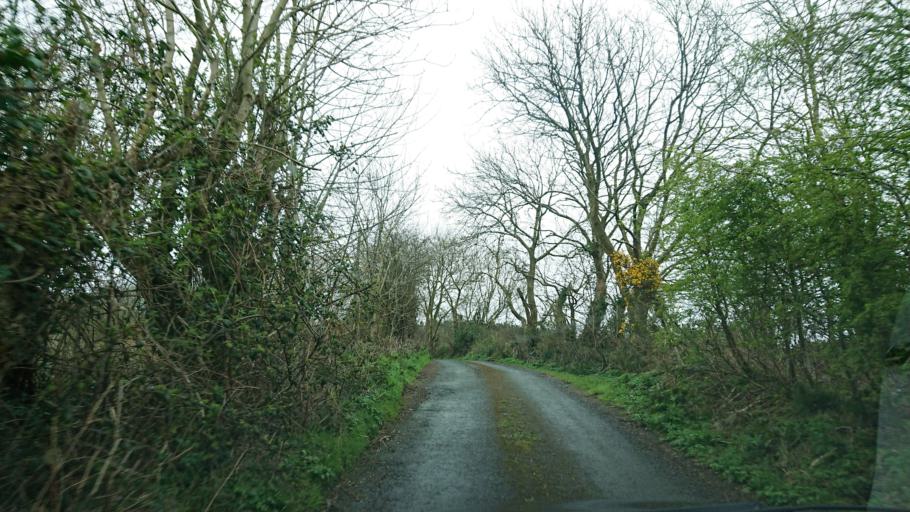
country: IE
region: Munster
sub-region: Waterford
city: Waterford
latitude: 52.2629
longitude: -7.0108
